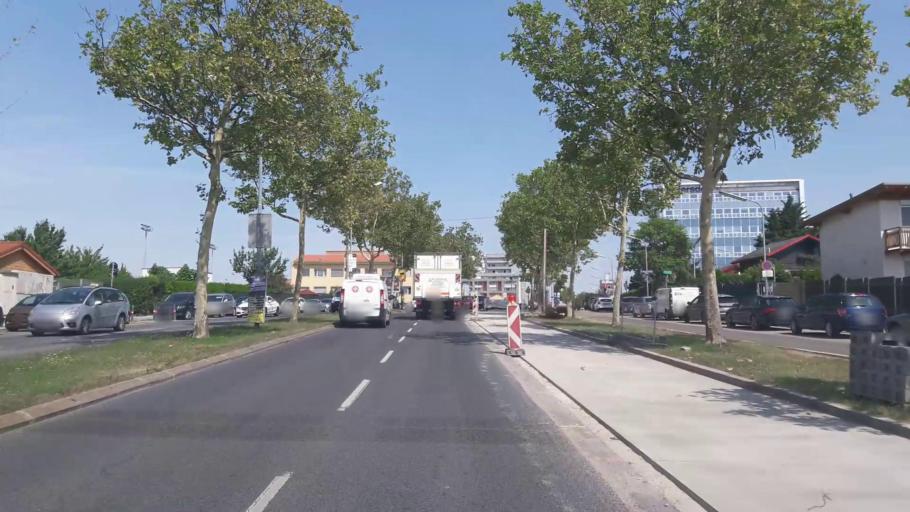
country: AT
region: Vienna
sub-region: Wien Stadt
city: Vienna
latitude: 48.1619
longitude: 16.3672
